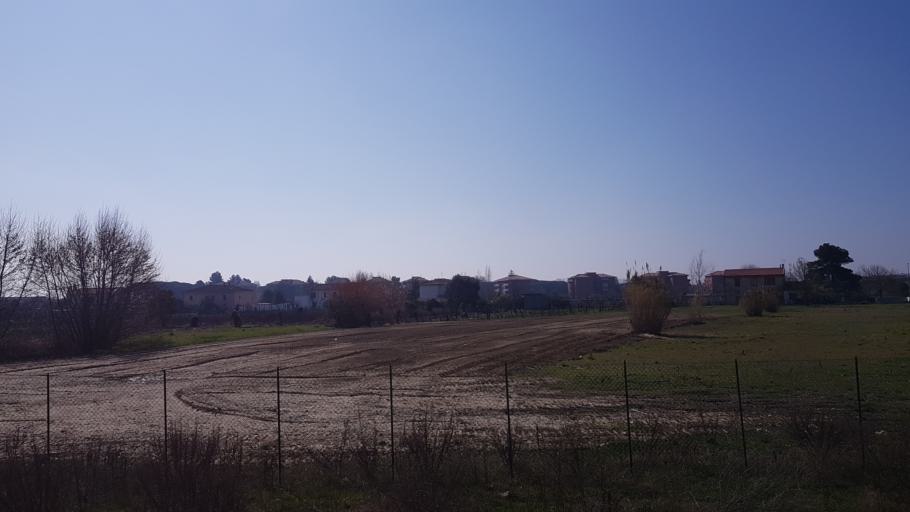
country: IT
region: Tuscany
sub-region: Province of Pisa
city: Pisa
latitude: 43.6991
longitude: 10.3924
